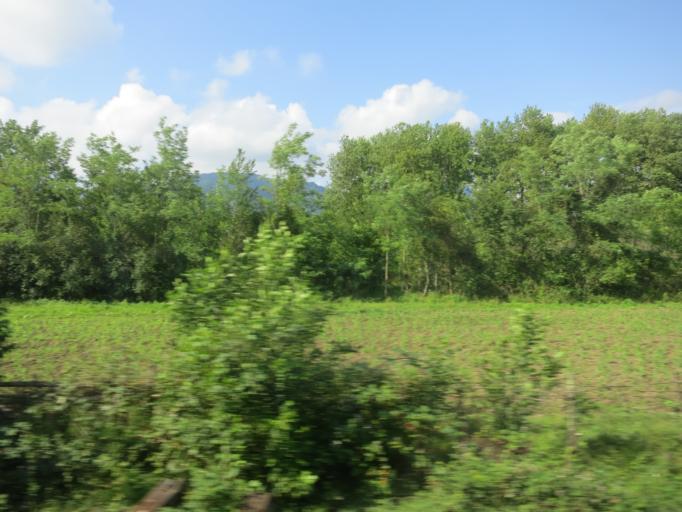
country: GE
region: Guria
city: Lanchkhuti
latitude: 42.0903
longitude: 42.0501
